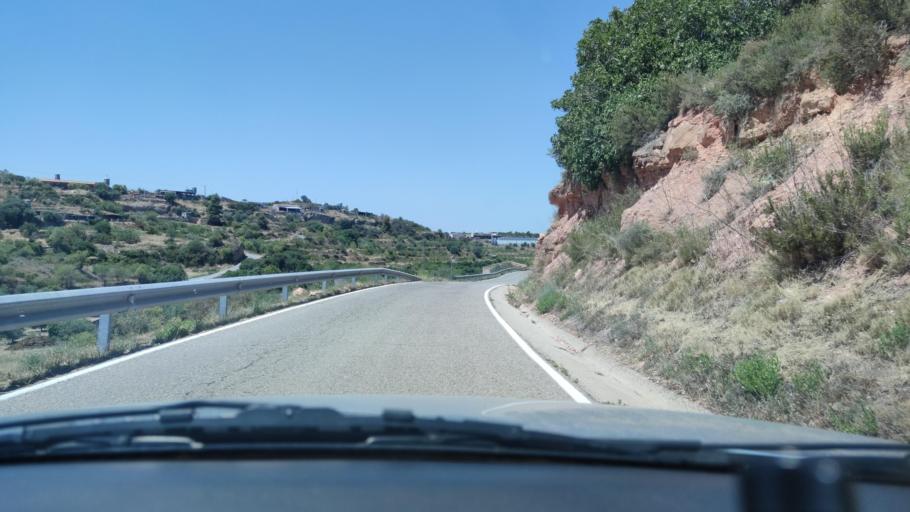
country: ES
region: Catalonia
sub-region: Provincia de Lleida
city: Juncosa
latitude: 41.3674
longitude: 0.7779
